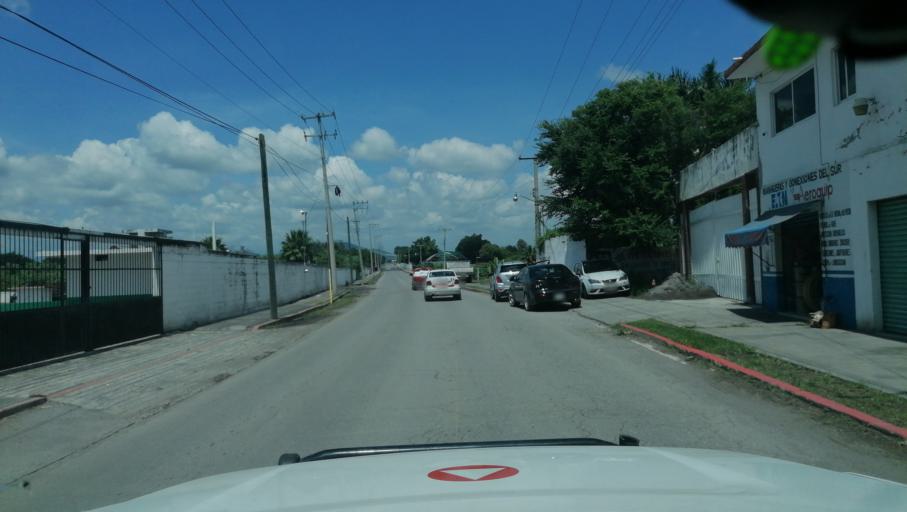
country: MX
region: Morelos
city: Zacatepec
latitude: 18.6476
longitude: -99.1840
